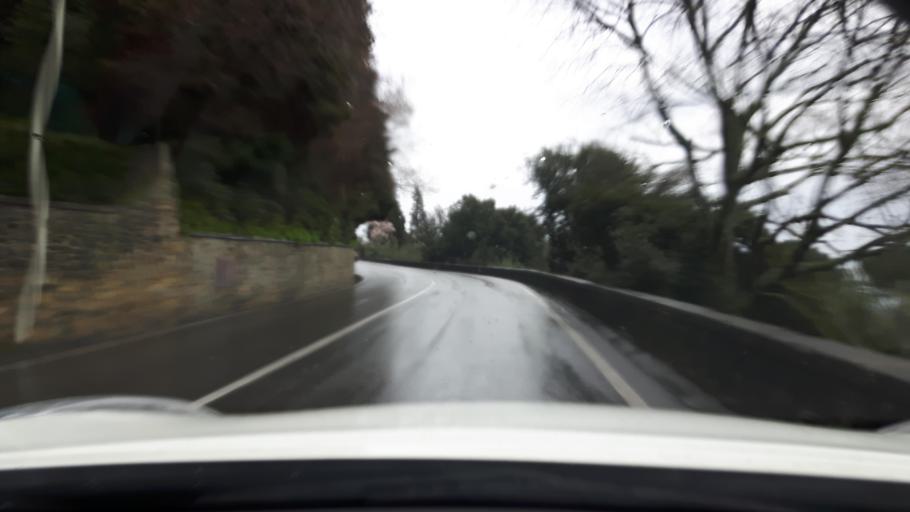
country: IT
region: Tuscany
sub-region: Province of Florence
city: Fiesole
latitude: 43.8013
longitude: 11.2910
